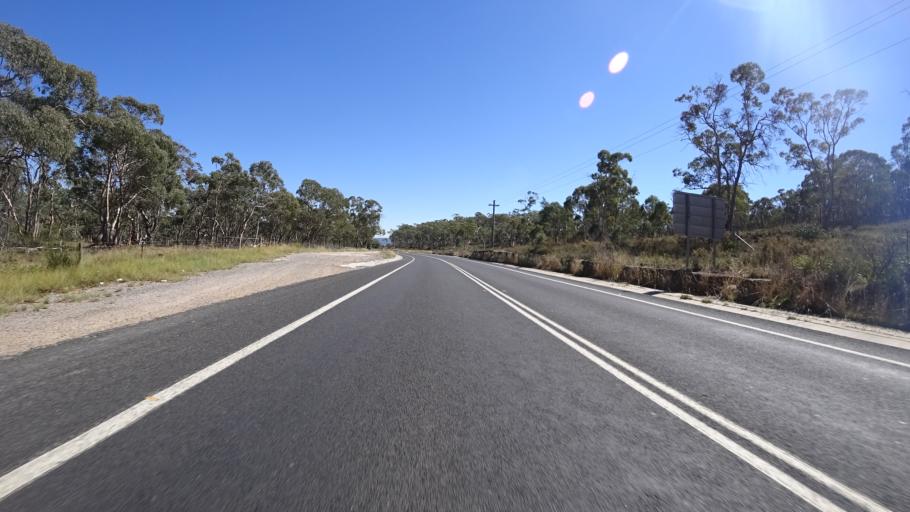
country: AU
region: New South Wales
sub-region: Lithgow
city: Lithgow
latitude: -33.4239
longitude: 150.1040
